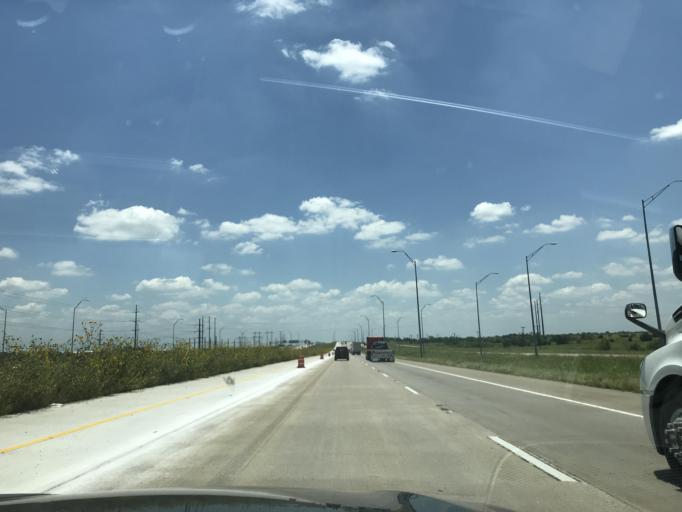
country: US
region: Texas
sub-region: Travis County
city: Manor
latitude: 30.3653
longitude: -97.5829
